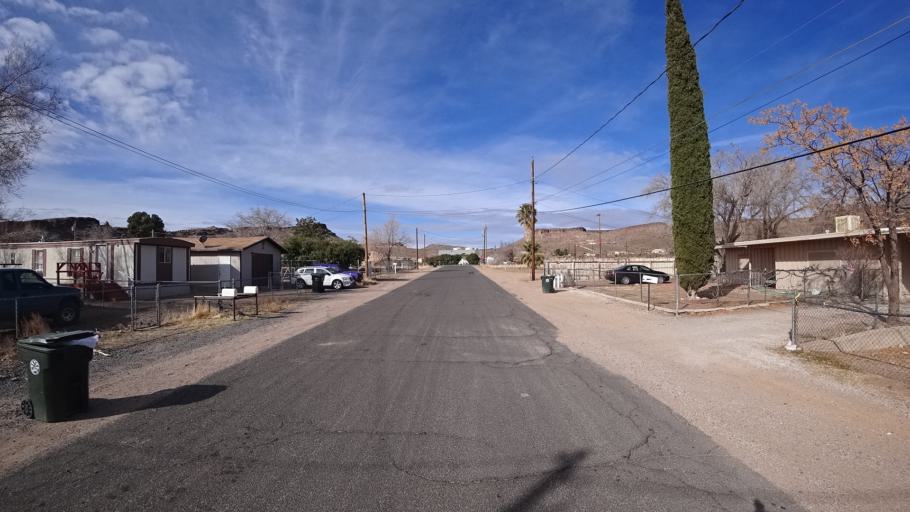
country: US
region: Arizona
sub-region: Mohave County
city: Kingman
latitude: 35.2164
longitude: -114.0514
